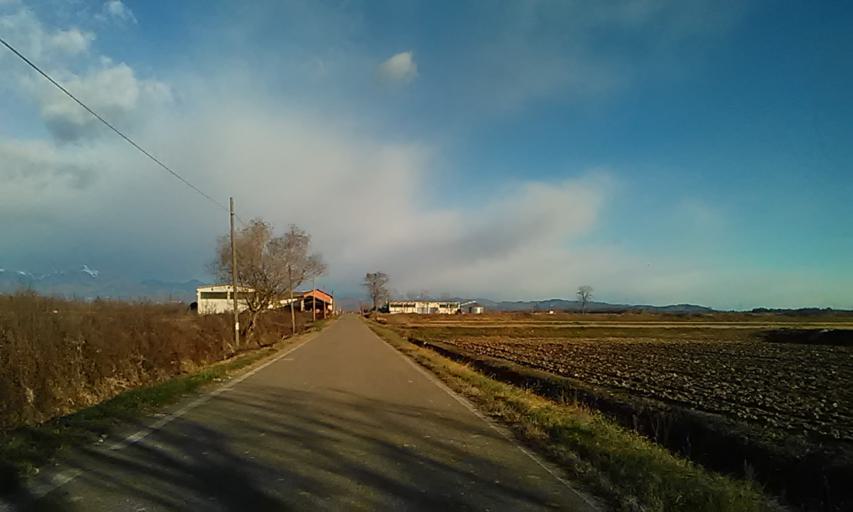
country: IT
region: Piedmont
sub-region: Provincia di Vercelli
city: Buronzo
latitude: 45.5020
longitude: 8.2701
